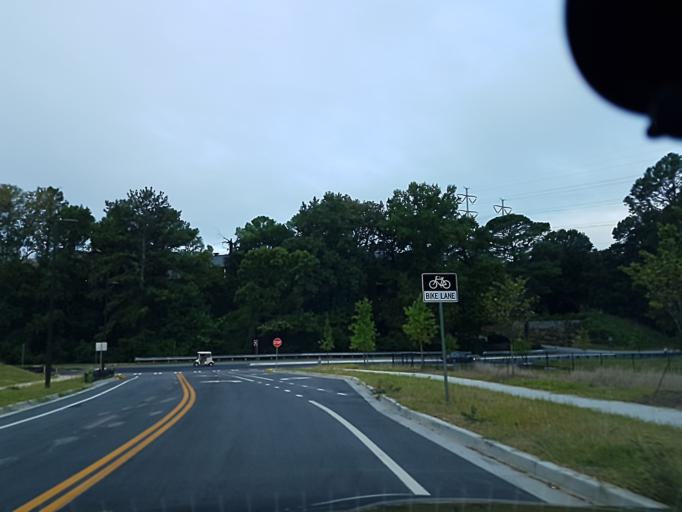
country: US
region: Georgia
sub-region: DeKalb County
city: North Druid Hills
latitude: 33.8265
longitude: -84.3366
